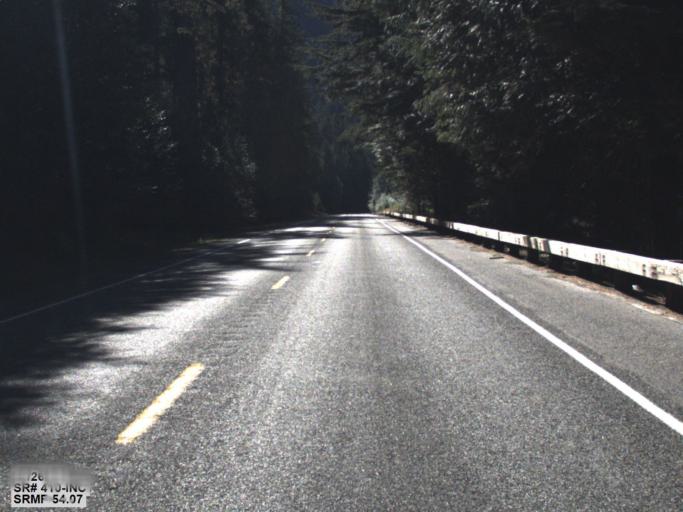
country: US
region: Washington
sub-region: King County
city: Enumclaw
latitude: 47.0256
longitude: -121.5399
